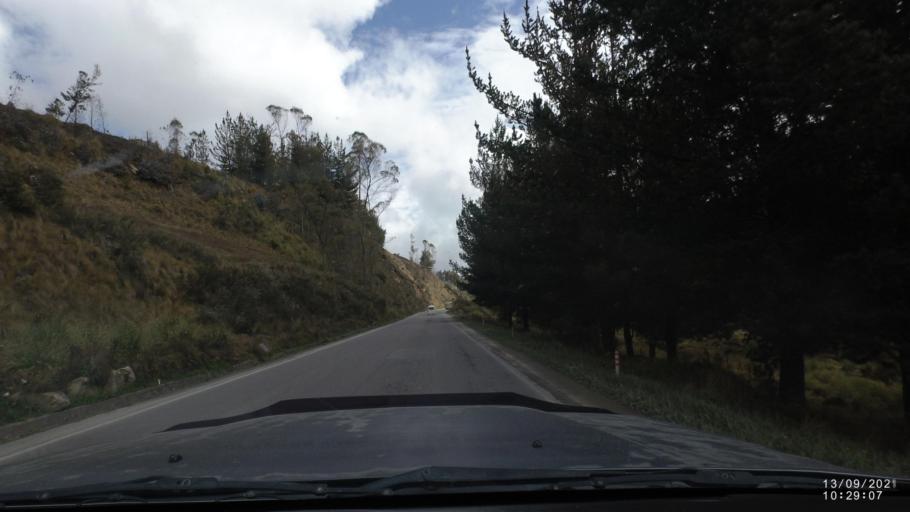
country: BO
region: Cochabamba
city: Colomi
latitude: -17.2720
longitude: -65.8773
